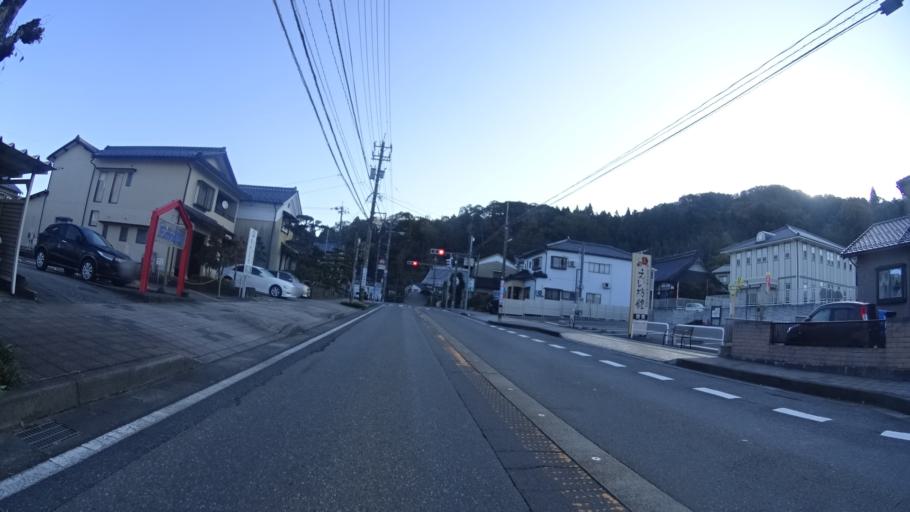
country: JP
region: Fukui
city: Maruoka
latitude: 36.0926
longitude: 136.3011
